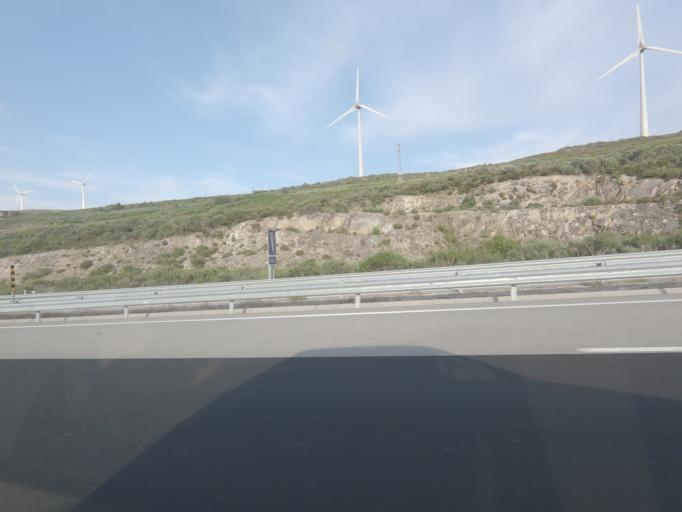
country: PT
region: Vila Real
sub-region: Vila Pouca de Aguiar
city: Vila Pouca de Aguiar
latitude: 41.4516
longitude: -7.6466
